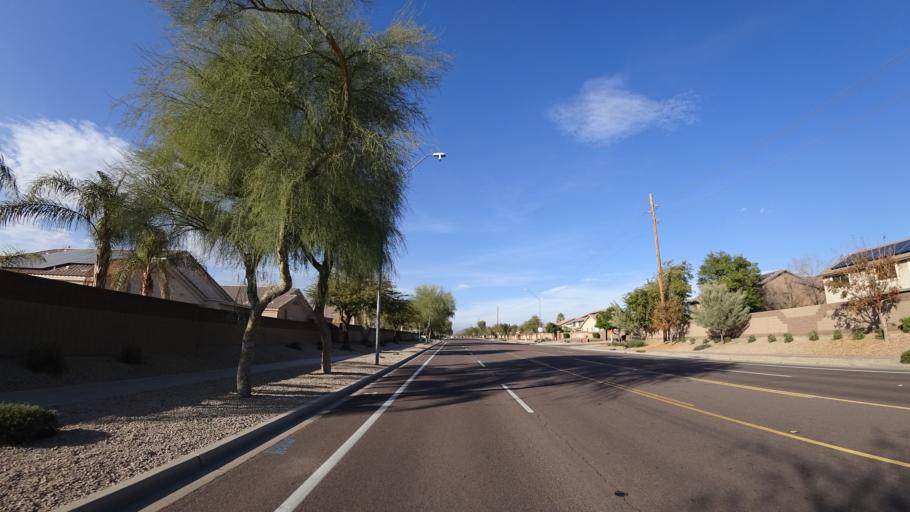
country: US
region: Arizona
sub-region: Maricopa County
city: Sun City
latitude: 33.6682
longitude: -112.2551
